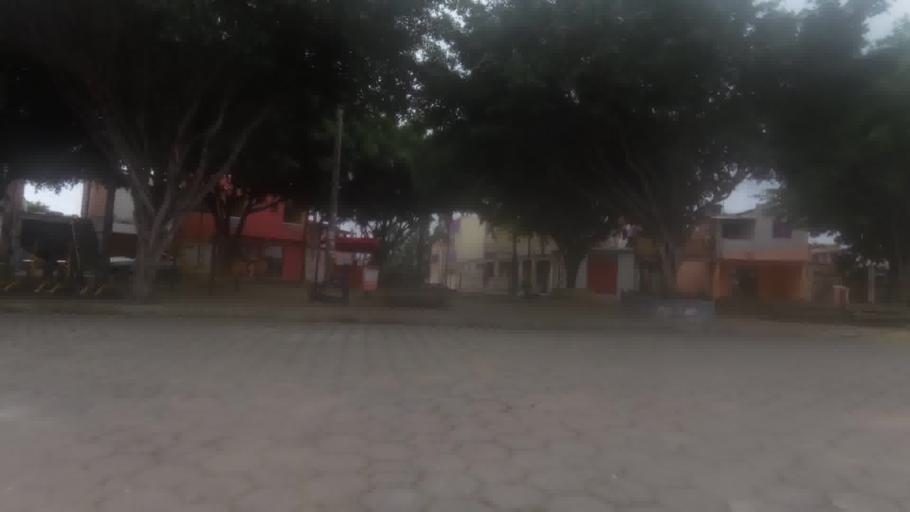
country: BR
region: Espirito Santo
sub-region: Piuma
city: Piuma
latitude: -20.7952
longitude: -40.6043
